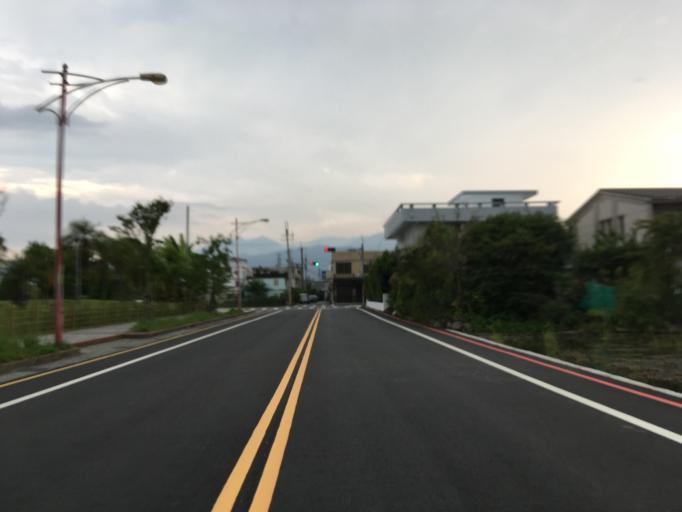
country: TW
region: Taiwan
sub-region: Yilan
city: Yilan
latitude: 24.6634
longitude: 121.7632
